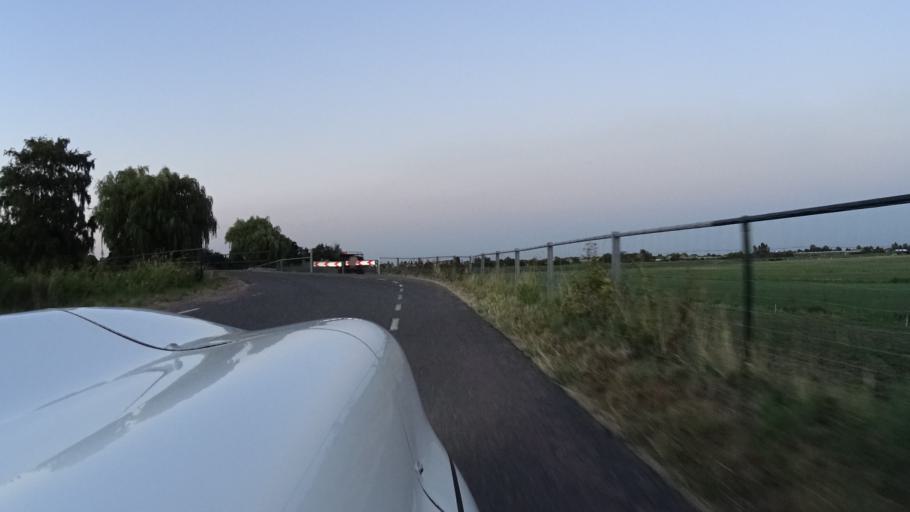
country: NL
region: South Holland
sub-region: Gemeente Kaag en Braassem
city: Oude Wetering
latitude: 52.1849
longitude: 4.6203
